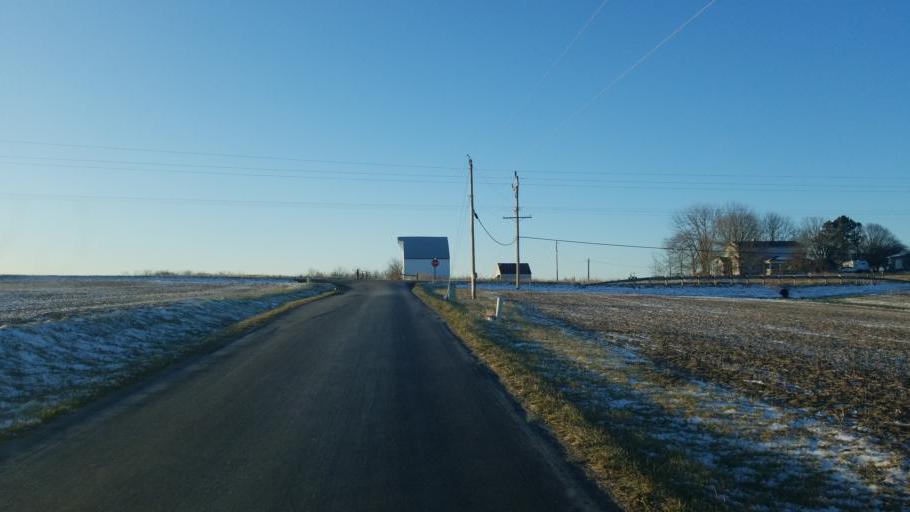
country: US
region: Ohio
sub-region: Highland County
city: Leesburg
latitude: 39.2413
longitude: -83.4971
